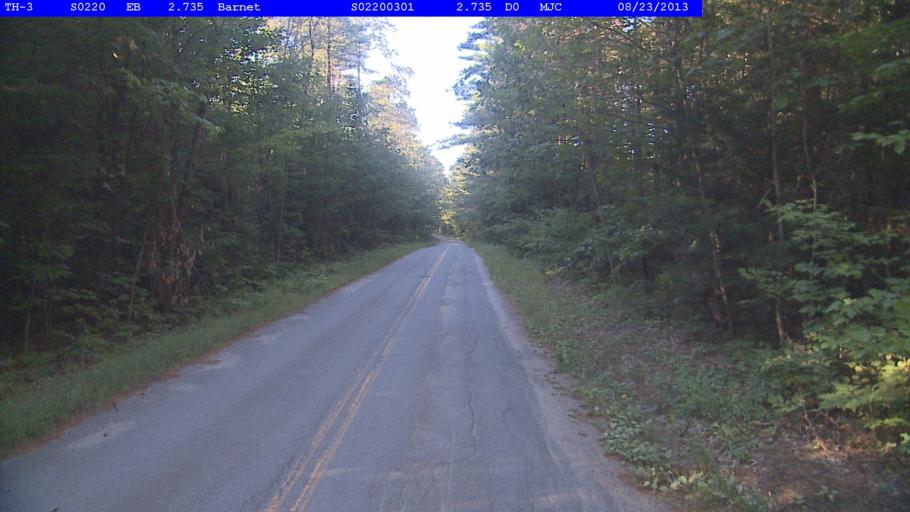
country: US
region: Vermont
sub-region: Caledonia County
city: Saint Johnsbury
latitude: 44.3335
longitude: -71.9982
